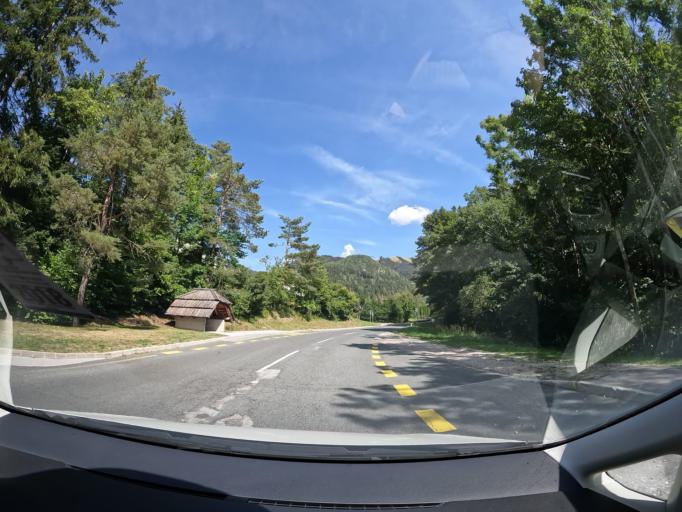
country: AT
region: Carinthia
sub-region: Politischer Bezirk Klagenfurt Land
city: Moosburg
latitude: 46.6613
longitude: 14.1300
